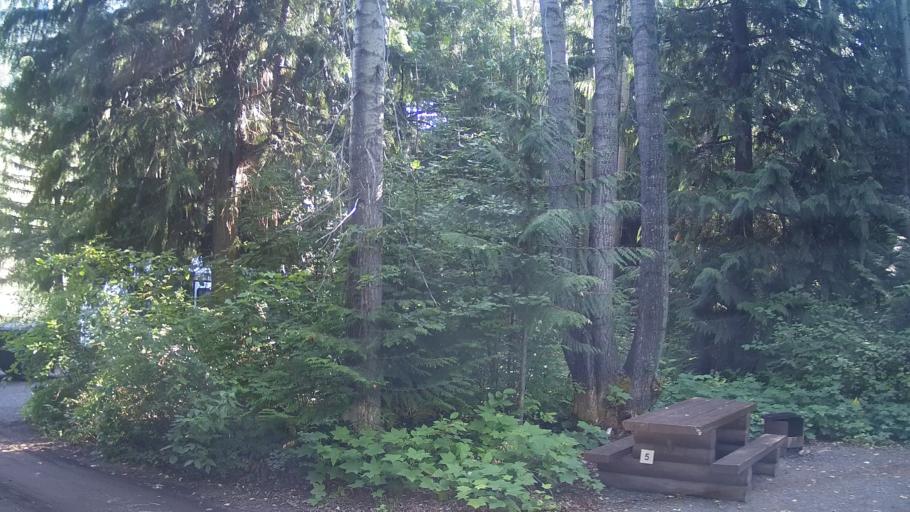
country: CA
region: British Columbia
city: Lillooet
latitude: 50.5359
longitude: -122.1351
